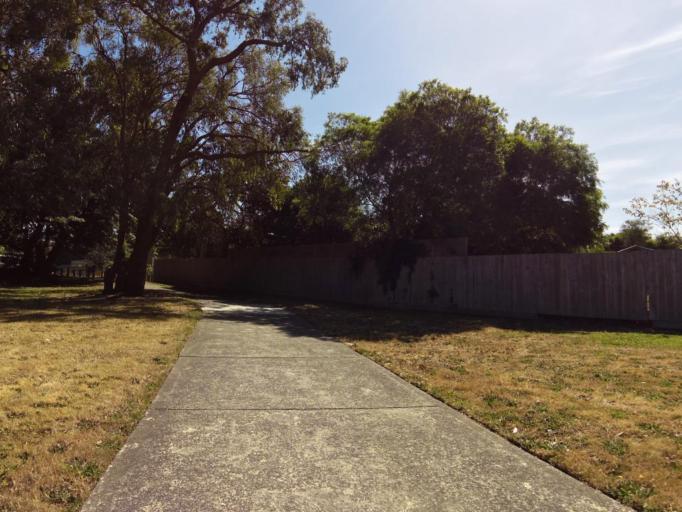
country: AU
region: Victoria
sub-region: Monash
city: Mulgrave
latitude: -37.8970
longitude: 145.1762
